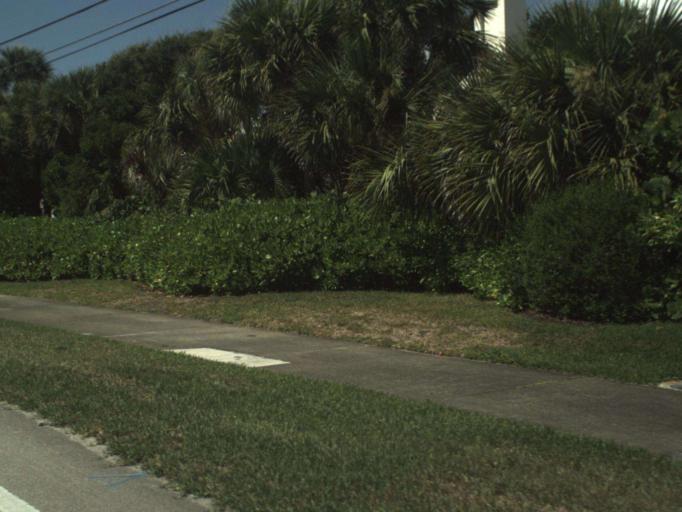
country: US
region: Florida
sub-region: Indian River County
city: Wabasso Beach
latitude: 27.7454
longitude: -80.3882
